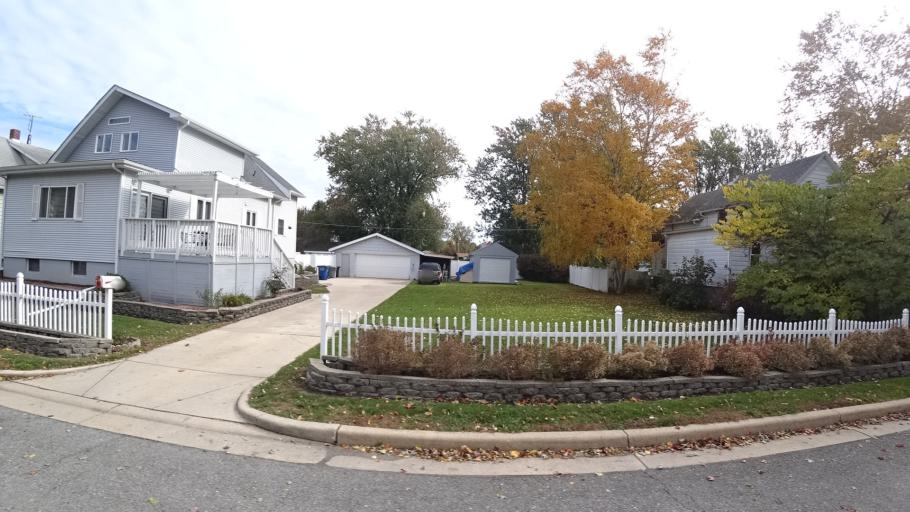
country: US
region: Indiana
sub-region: LaPorte County
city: Michigan City
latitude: 41.7020
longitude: -86.8996
